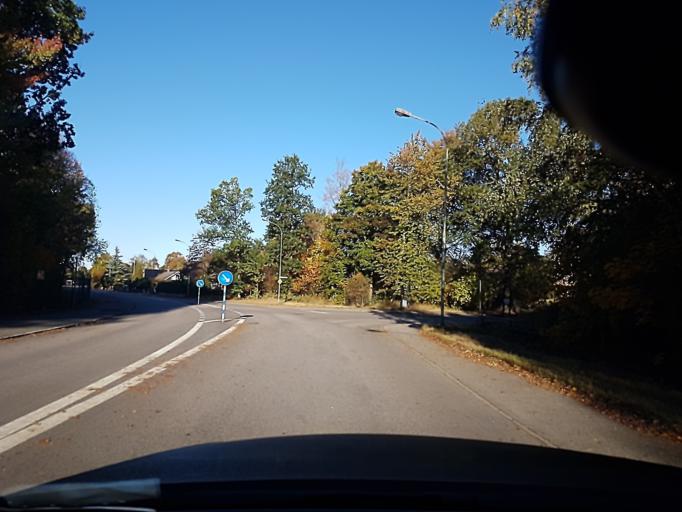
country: SE
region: Kronoberg
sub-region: Vaxjo Kommun
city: Vaexjoe
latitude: 56.8709
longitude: 14.8343
